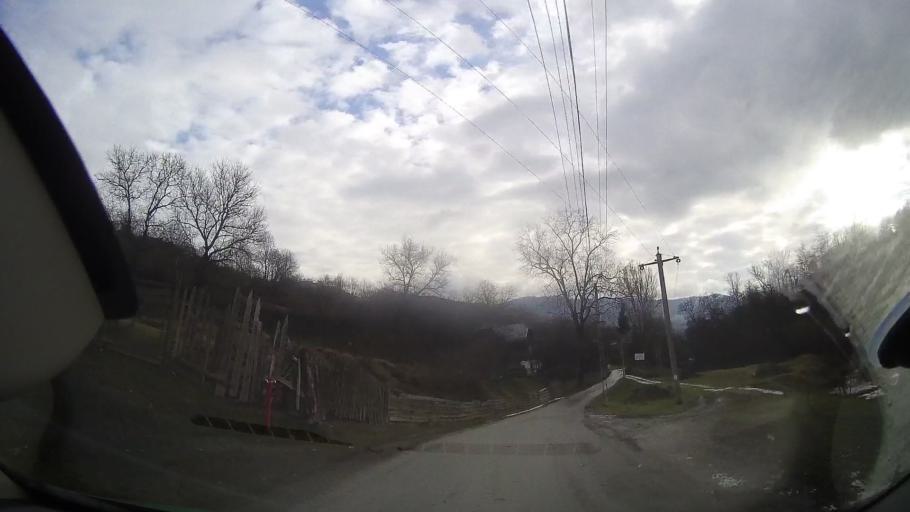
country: RO
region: Alba
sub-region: Comuna Ocolis
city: Ocolis
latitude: 46.4973
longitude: 23.4539
